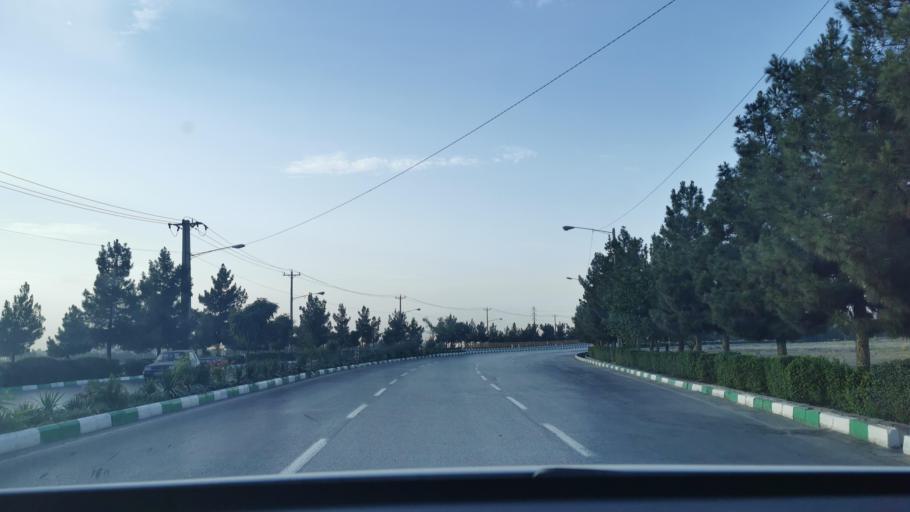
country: IR
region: Razavi Khorasan
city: Mashhad
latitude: 36.3491
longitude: 59.5396
